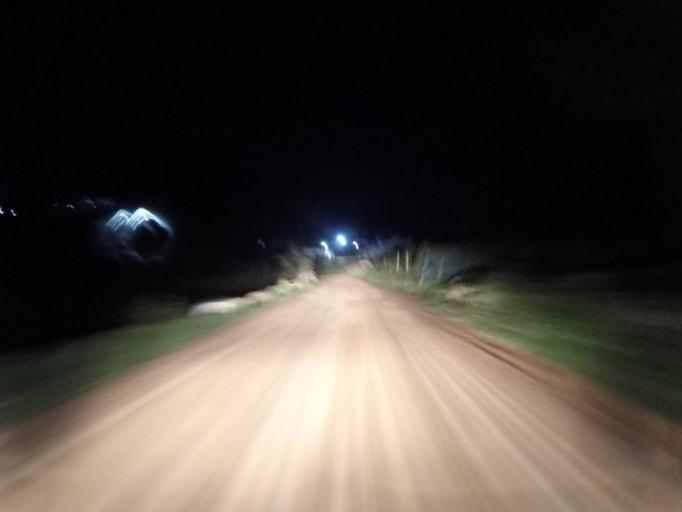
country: IN
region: Tamil Nadu
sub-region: Nilgiri
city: Kotagiri
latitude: 11.4514
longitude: 76.8719
